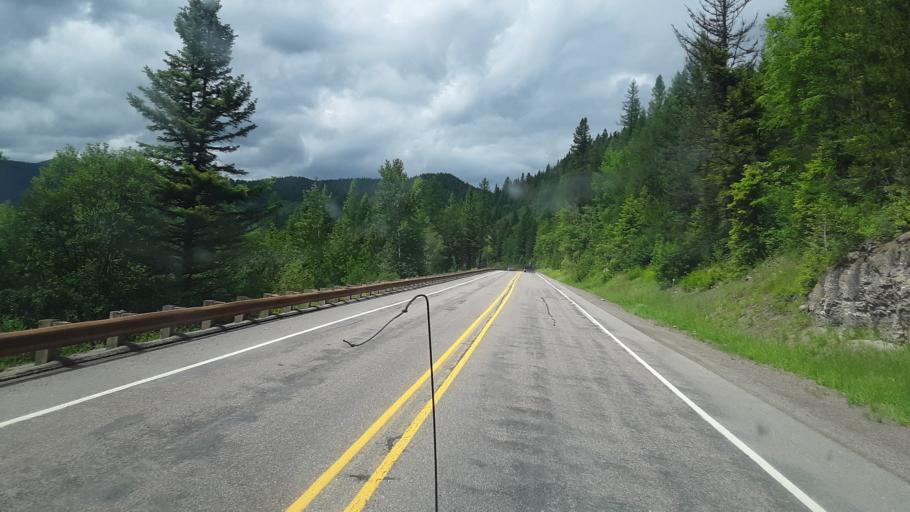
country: US
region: Montana
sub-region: Flathead County
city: Bigfork
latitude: 48.2530
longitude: -113.5692
